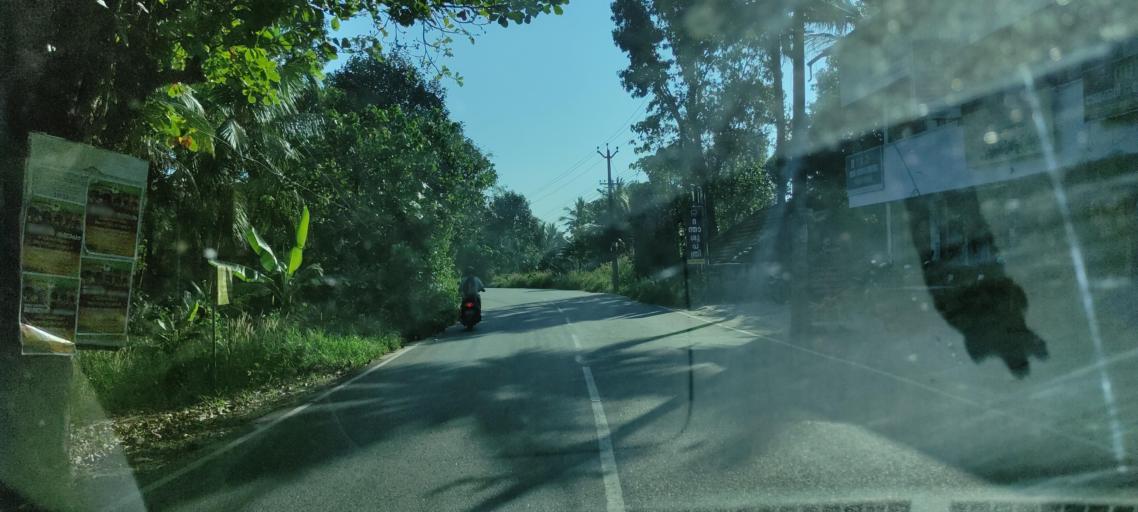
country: IN
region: Kerala
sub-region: Pattanamtitta
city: Adur
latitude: 9.2035
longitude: 76.7453
